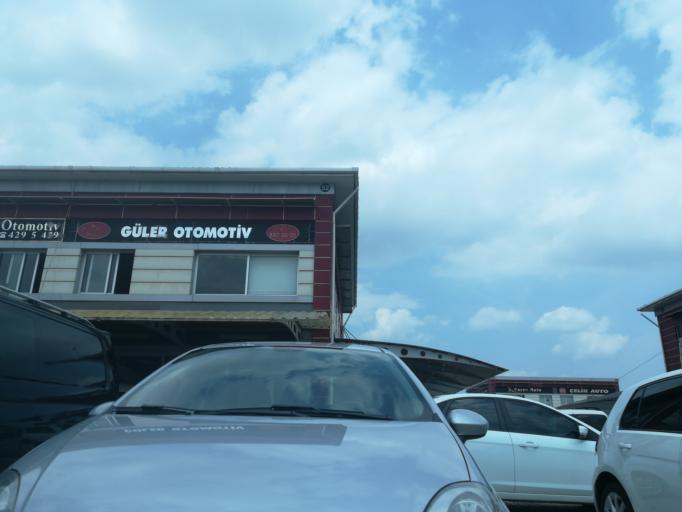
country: TR
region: Adana
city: Seyhan
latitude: 37.0015
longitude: 35.2461
